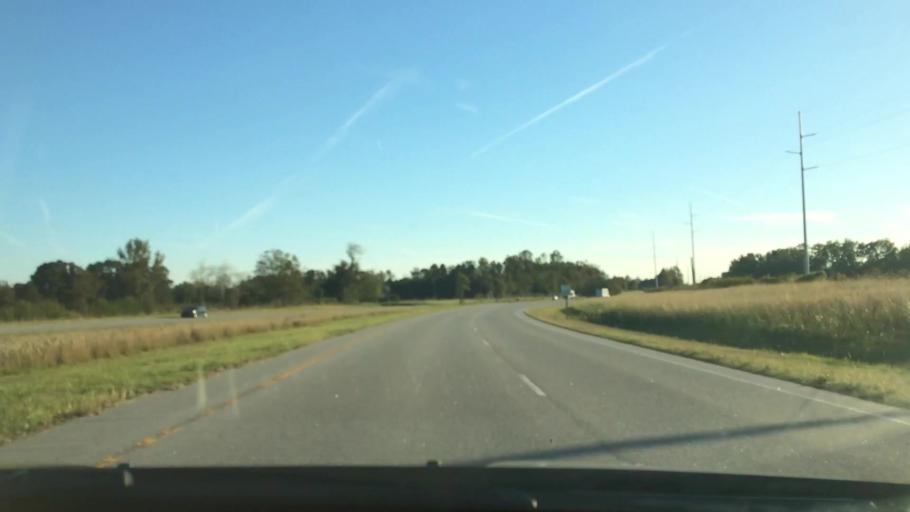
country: US
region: North Carolina
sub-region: Pitt County
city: Grifton
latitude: 35.4041
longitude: -77.4366
